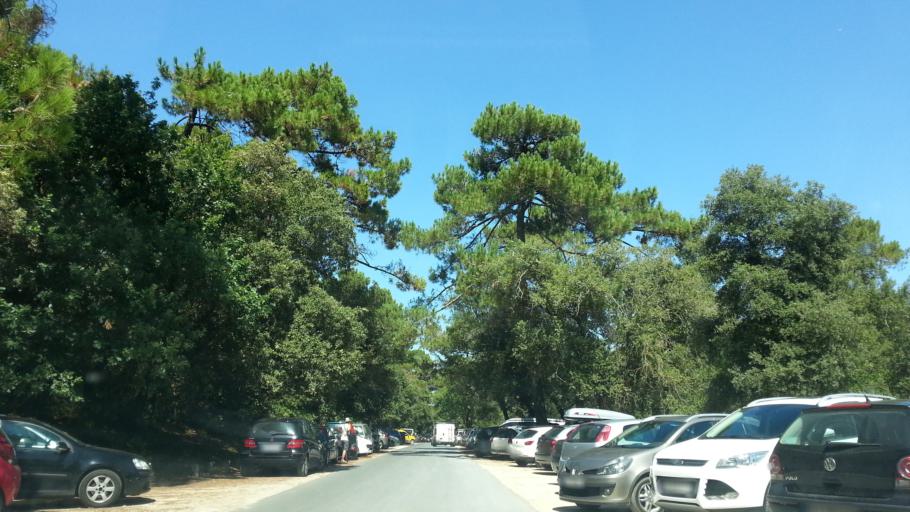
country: FR
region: Poitou-Charentes
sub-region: Departement de la Charente-Maritime
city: Dolus-d'Oleron
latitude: 45.8787
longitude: -1.2596
